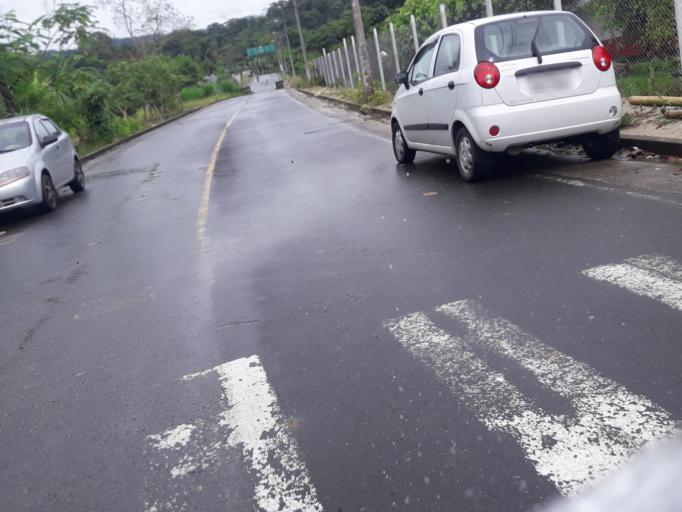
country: EC
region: Napo
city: Tena
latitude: -0.9669
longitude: -77.8539
